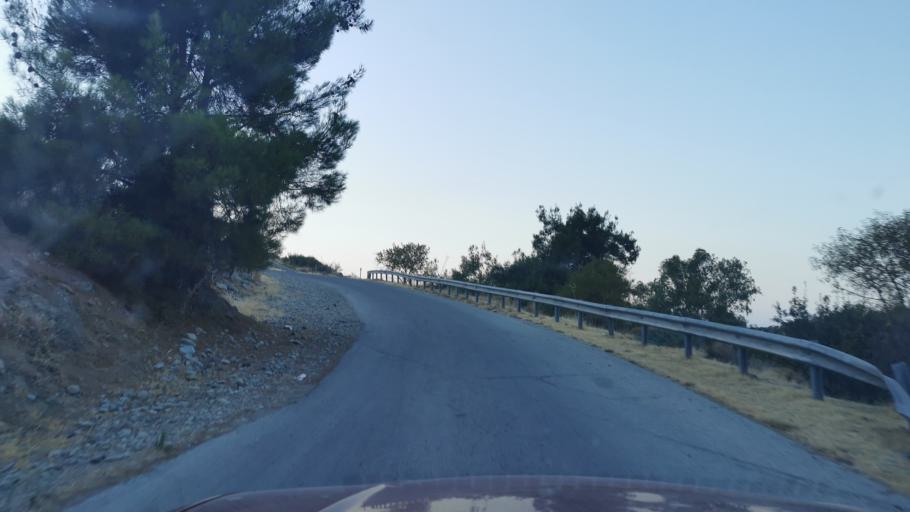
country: CY
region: Lefkosia
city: Peristerona
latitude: 35.0606
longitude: 33.0799
